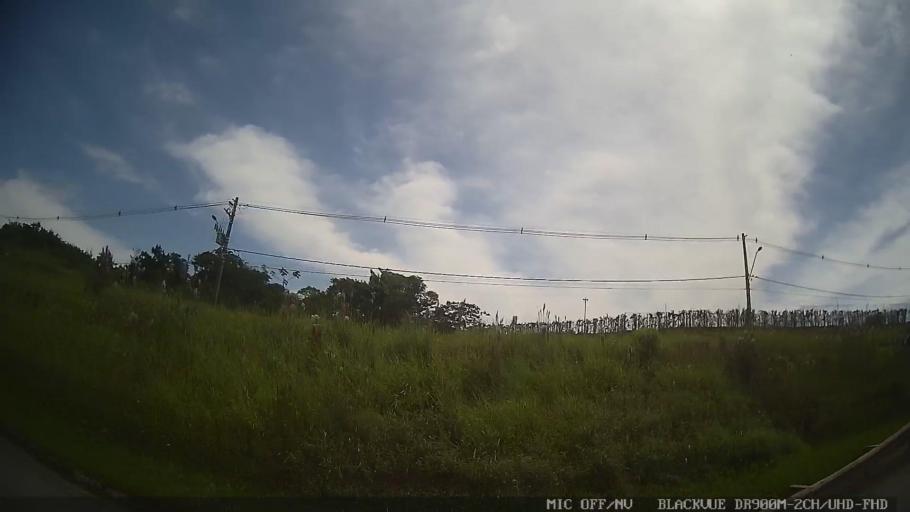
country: BR
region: Sao Paulo
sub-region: Aruja
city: Aruja
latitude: -23.4385
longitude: -46.2598
